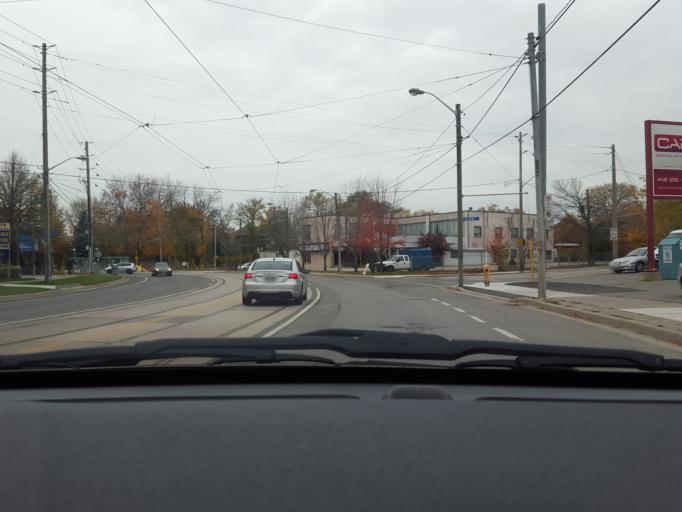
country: CA
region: Ontario
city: Etobicoke
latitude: 43.6200
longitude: -79.4850
